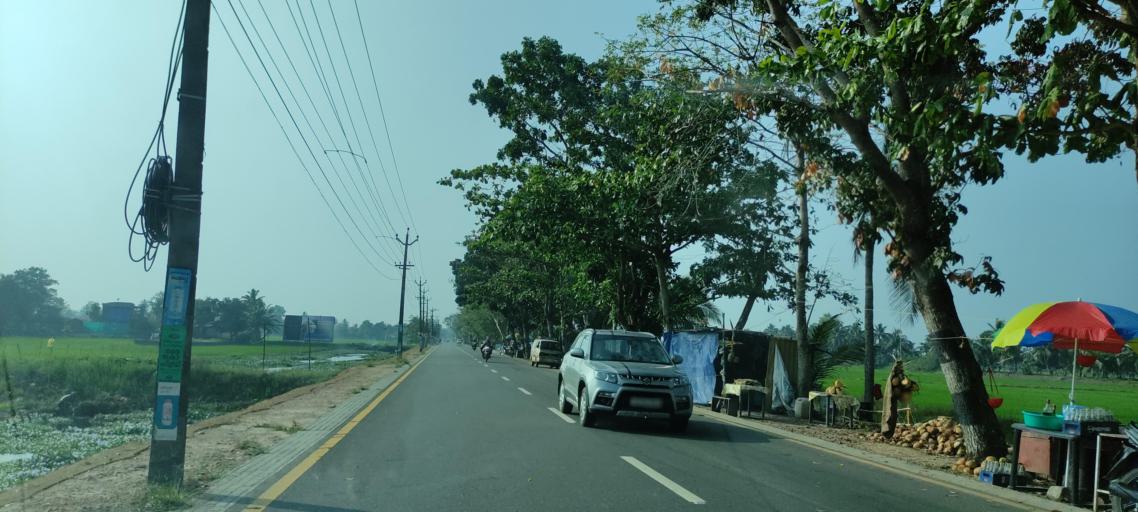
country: IN
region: Kerala
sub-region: Kottayam
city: Changanacheri
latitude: 9.3663
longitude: 76.4368
